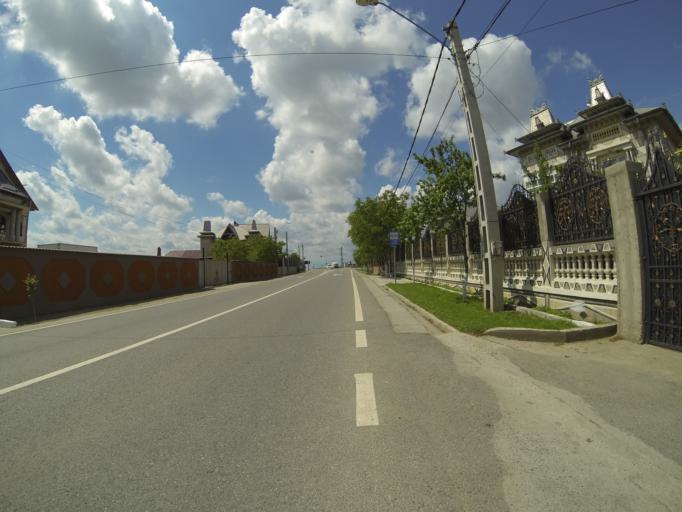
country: RO
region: Dolj
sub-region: Comuna Carcea
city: Carcea
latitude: 44.2638
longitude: 23.9010
